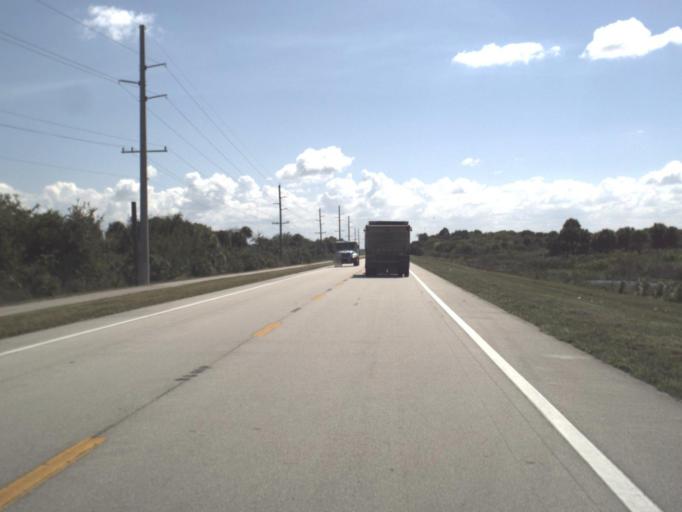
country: US
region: Florida
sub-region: Glades County
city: Moore Haven
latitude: 26.9326
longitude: -81.1223
